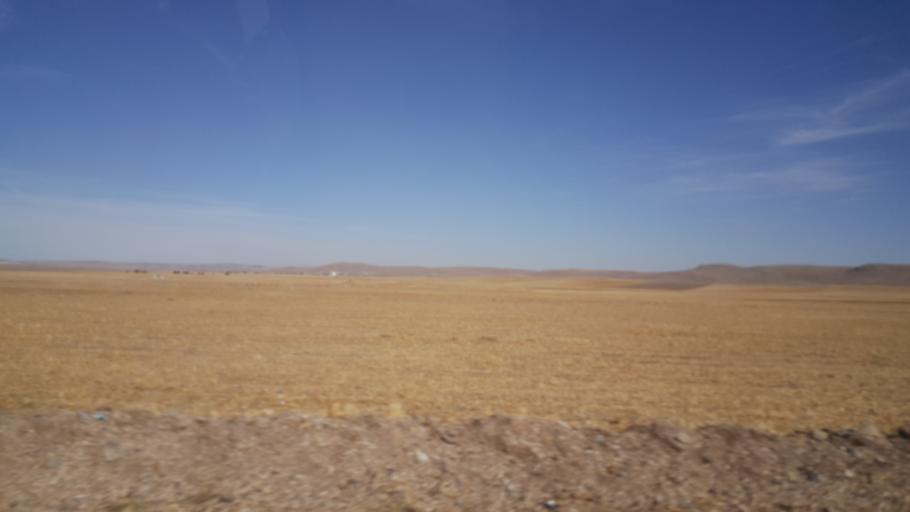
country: TR
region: Ankara
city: Yenice
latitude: 39.3342
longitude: 32.7501
